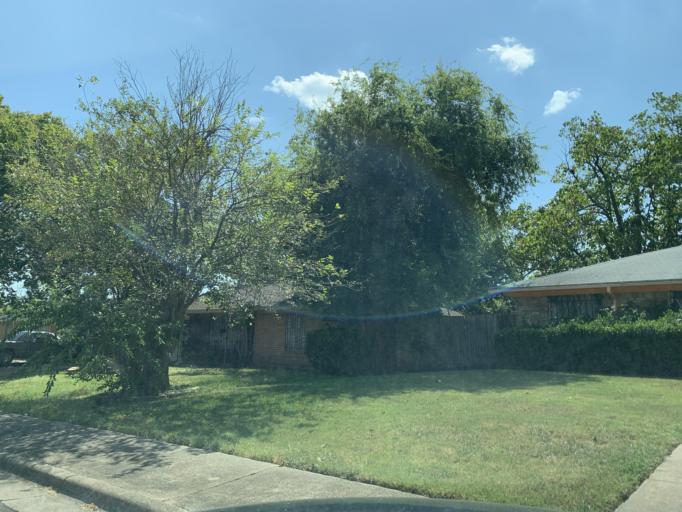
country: US
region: Texas
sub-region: Dallas County
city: Hutchins
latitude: 32.6748
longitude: -96.8026
